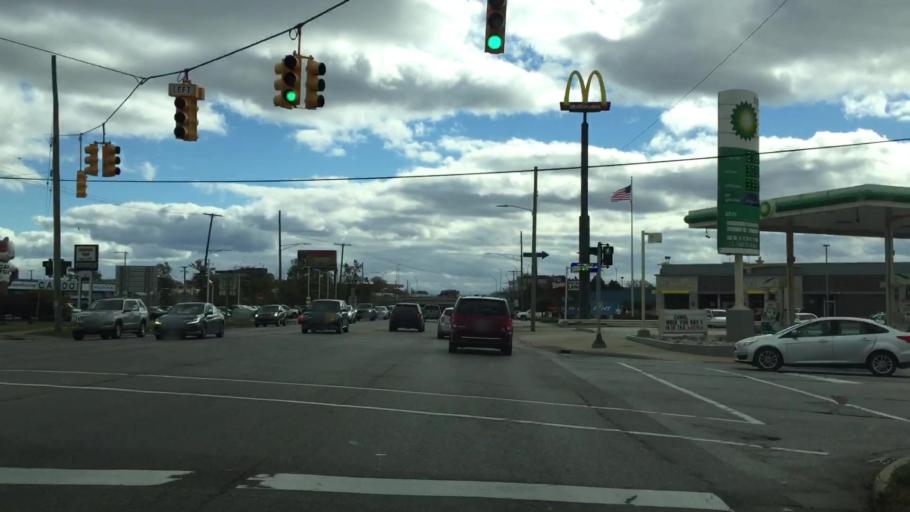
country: US
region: Michigan
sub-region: Saint Clair County
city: Port Huron
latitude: 43.0018
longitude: -82.4393
